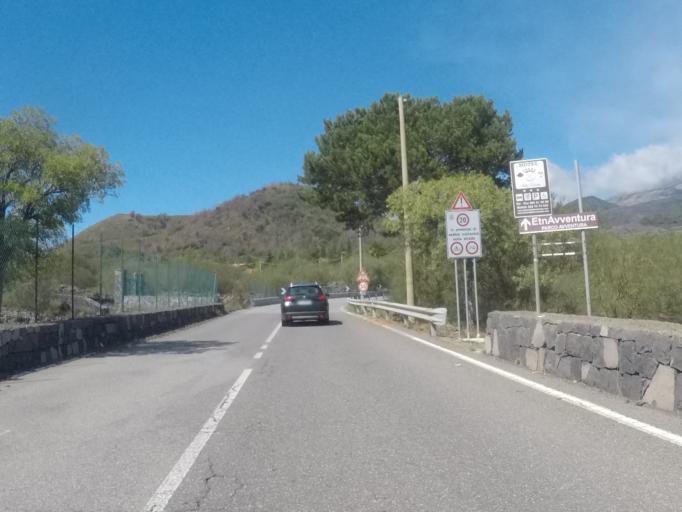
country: IT
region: Sicily
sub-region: Catania
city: Ragalna
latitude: 37.6506
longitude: 14.9894
